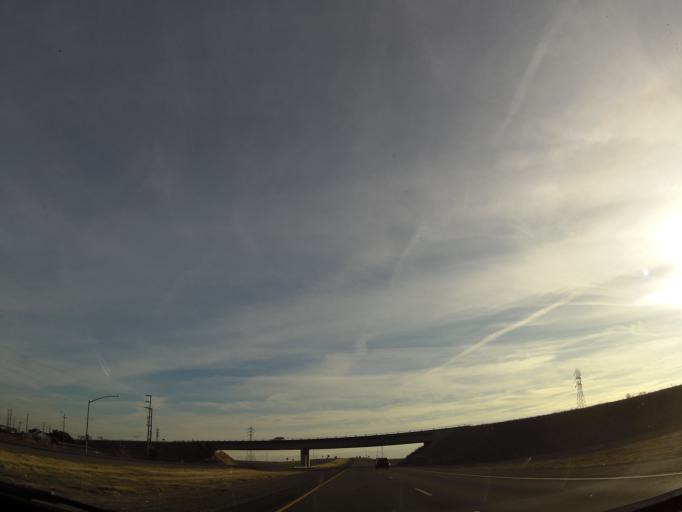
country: US
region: California
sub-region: San Joaquin County
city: Tracy
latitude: 37.7496
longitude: -121.3439
